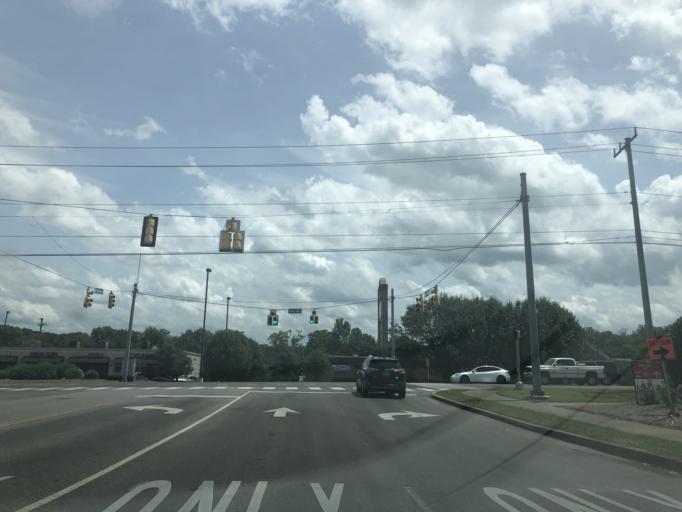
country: US
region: Tennessee
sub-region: Cheatham County
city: Pegram
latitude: 36.0449
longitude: -86.9563
